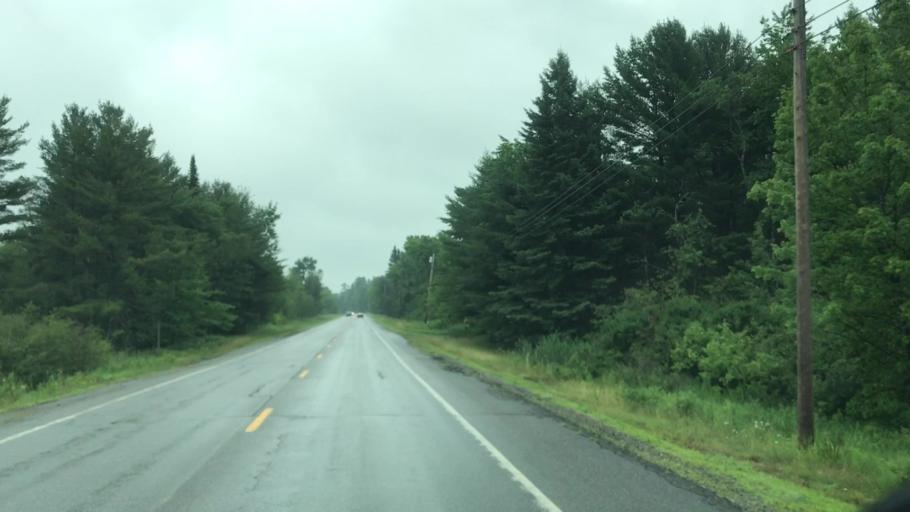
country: US
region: Maine
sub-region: Penobscot County
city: Howland
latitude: 45.2463
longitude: -68.6396
